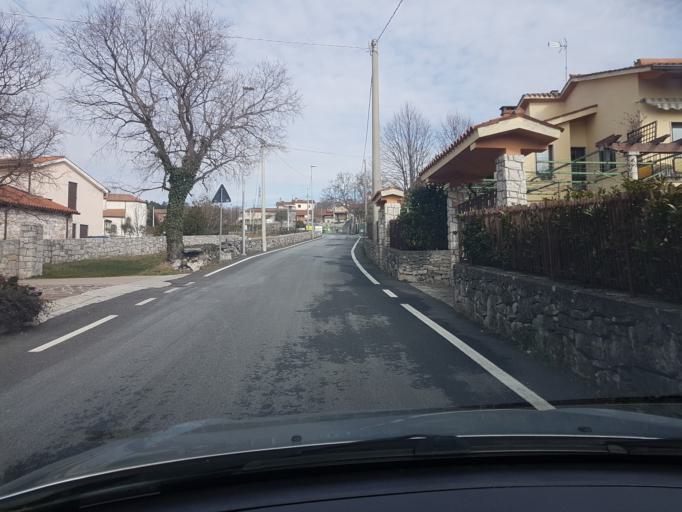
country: IT
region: Friuli Venezia Giulia
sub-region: Provincia di Trieste
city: Aurisina Cave
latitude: 45.7693
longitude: 13.6655
